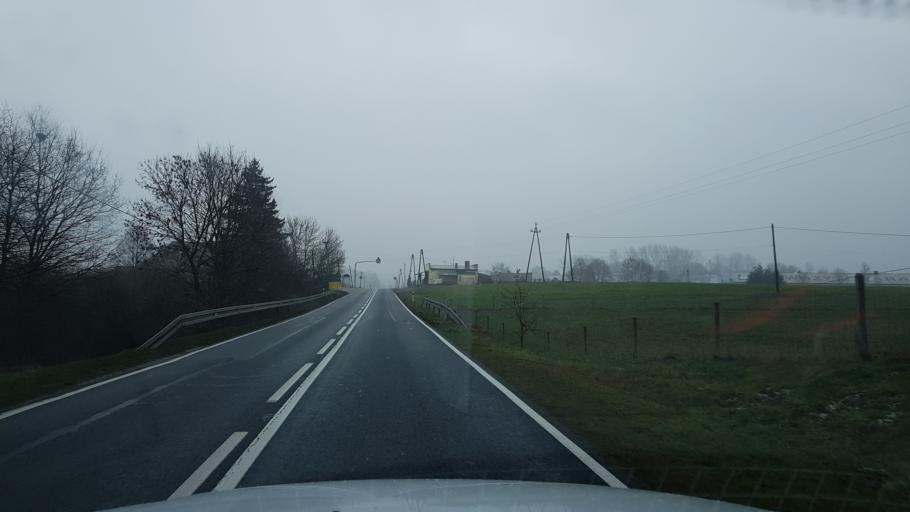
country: PL
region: West Pomeranian Voivodeship
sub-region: Powiat lobeski
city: Wegorzyno
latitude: 53.5162
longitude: 15.6383
